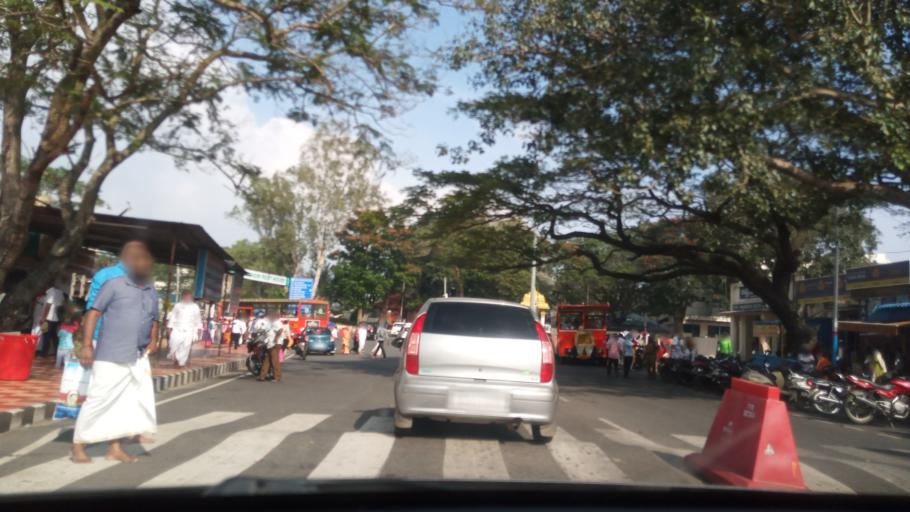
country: IN
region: Andhra Pradesh
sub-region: Chittoor
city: Tirumala
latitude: 13.6806
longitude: 79.3503
